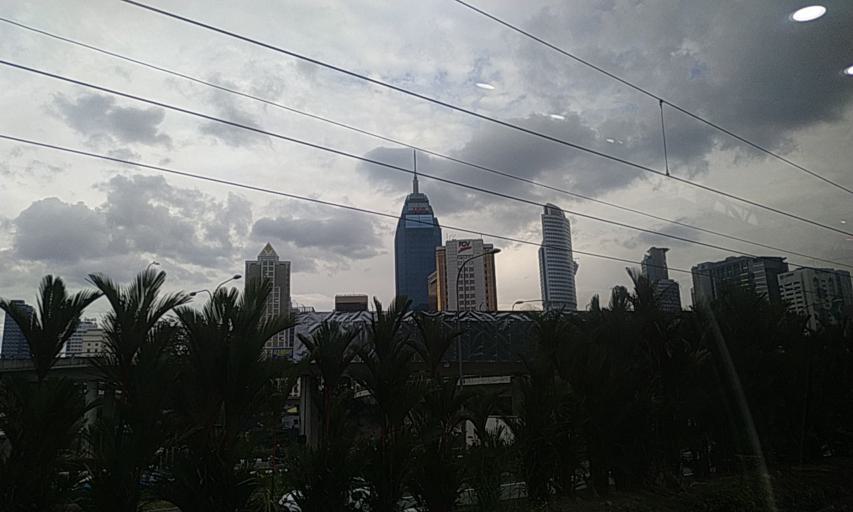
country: MY
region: Kuala Lumpur
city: Kuala Lumpur
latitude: 3.1637
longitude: 101.6920
